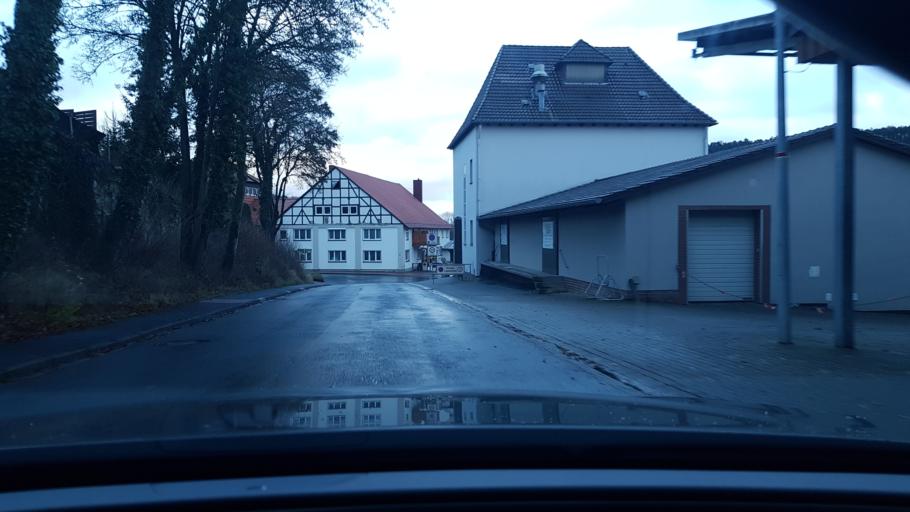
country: DE
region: Lower Saxony
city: Hardegsen
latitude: 51.6498
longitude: 9.8251
